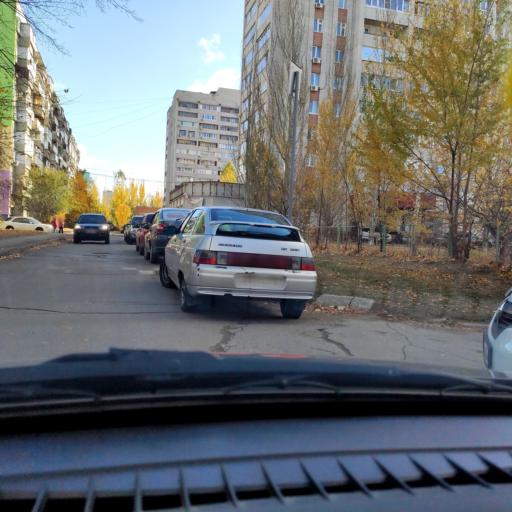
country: RU
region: Samara
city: Tol'yatti
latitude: 53.5390
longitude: 49.3353
